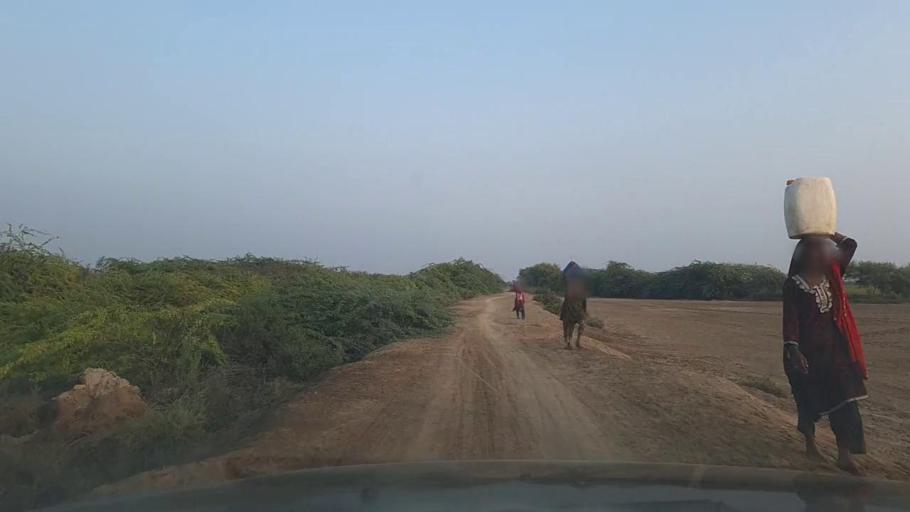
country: PK
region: Sindh
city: Jati
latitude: 24.5393
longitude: 68.4026
